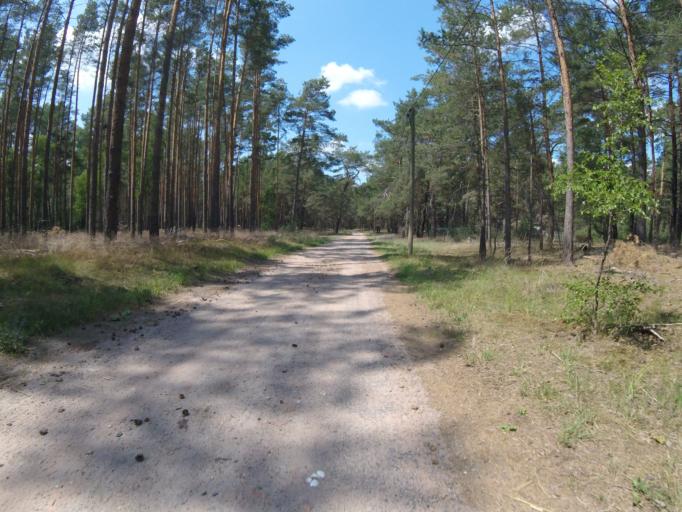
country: DE
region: Brandenburg
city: Bestensee
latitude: 52.2493
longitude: 13.6862
